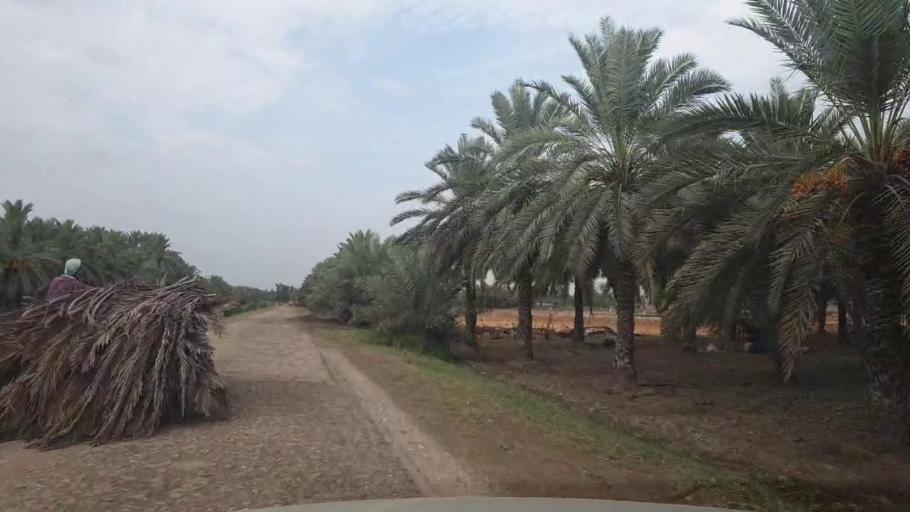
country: PK
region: Sindh
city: Khairpur
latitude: 27.6040
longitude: 68.8318
